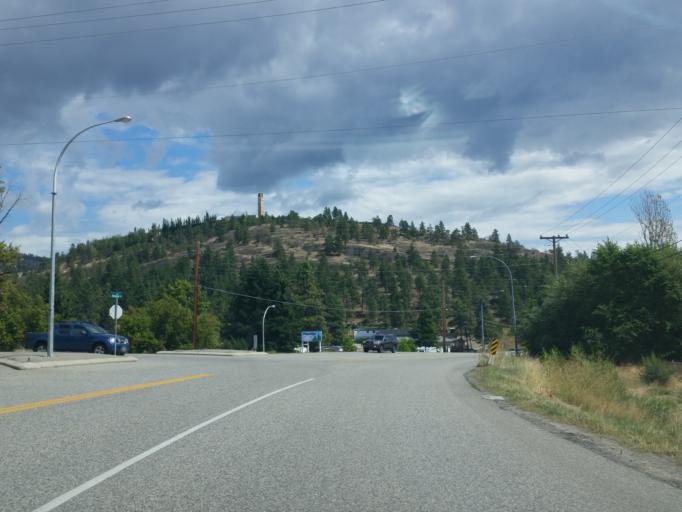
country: CA
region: British Columbia
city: West Kelowna
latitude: 49.8313
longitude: -119.5952
